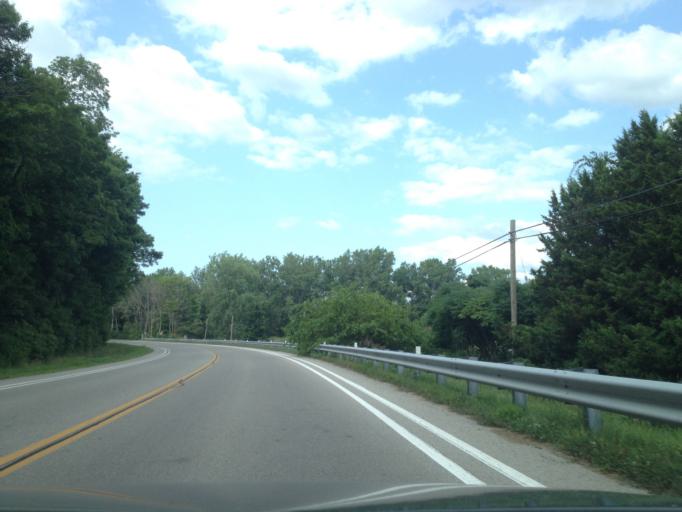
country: CA
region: Ontario
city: Aylmer
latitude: 42.6664
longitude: -80.9871
